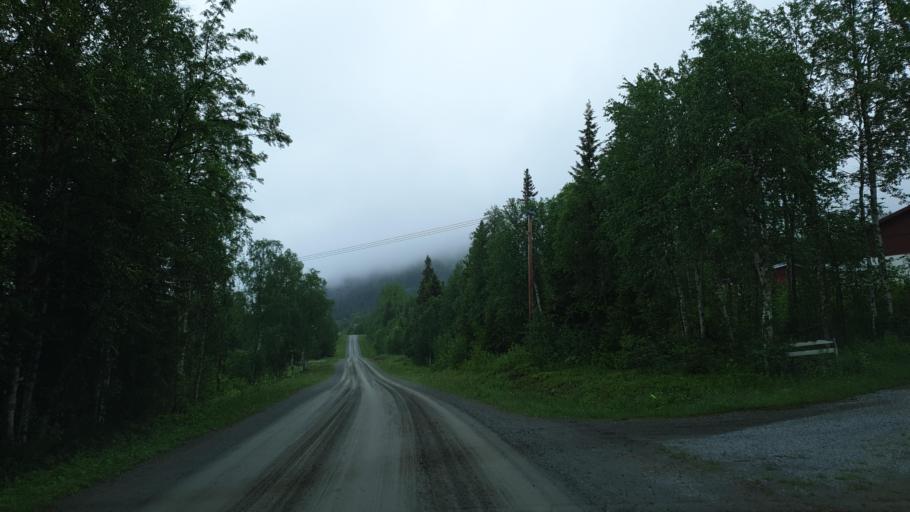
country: SE
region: Vaesterbotten
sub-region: Vilhelmina Kommun
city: Sjoberg
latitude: 65.3426
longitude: 15.8706
